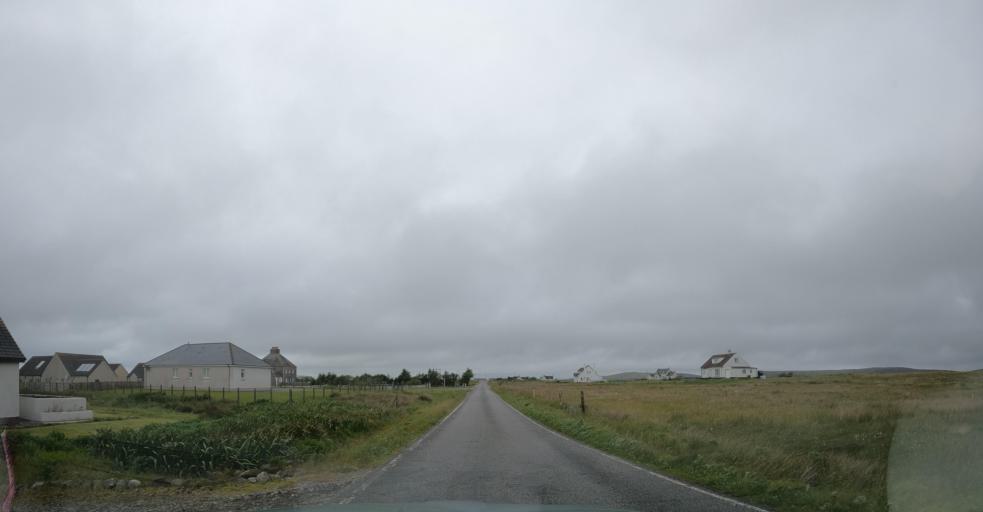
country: GB
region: Scotland
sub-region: Eilean Siar
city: Isle of North Uist
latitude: 57.5701
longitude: -7.3946
